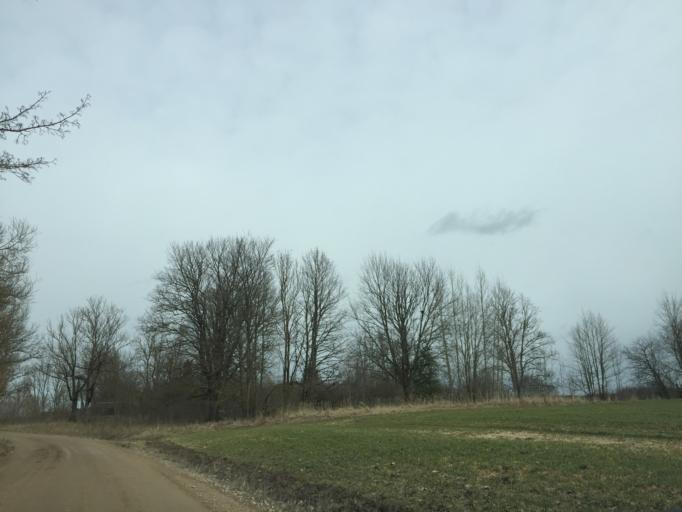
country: LV
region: Jekabpils Rajons
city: Jekabpils
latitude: 56.4747
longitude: 26.0346
